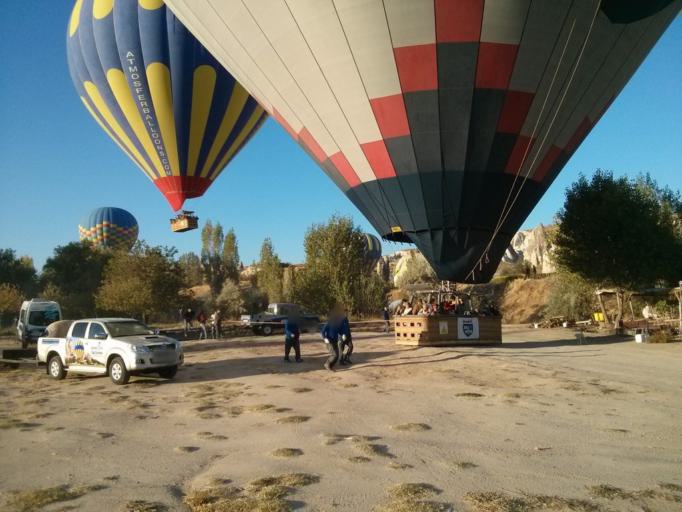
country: TR
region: Nevsehir
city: Goereme
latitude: 38.6443
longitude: 34.8360
